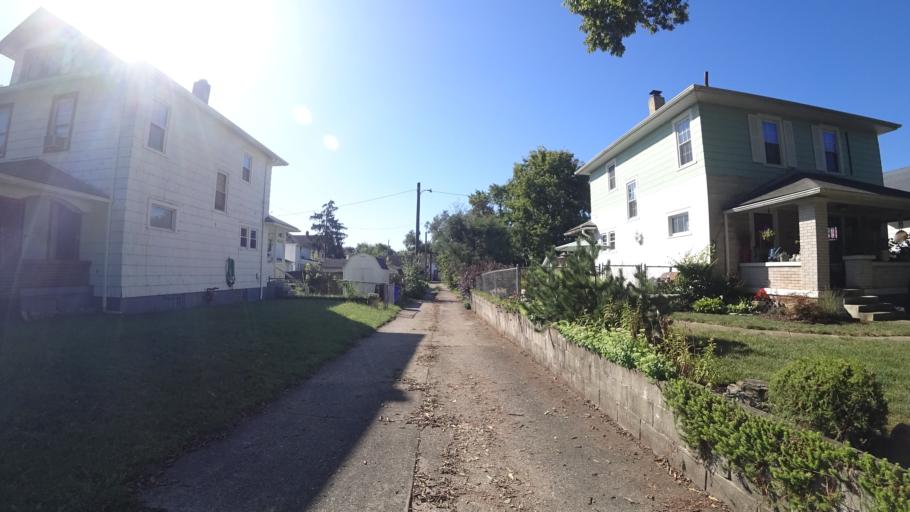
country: US
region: Ohio
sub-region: Butler County
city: Hamilton
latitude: 39.4074
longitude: -84.5460
